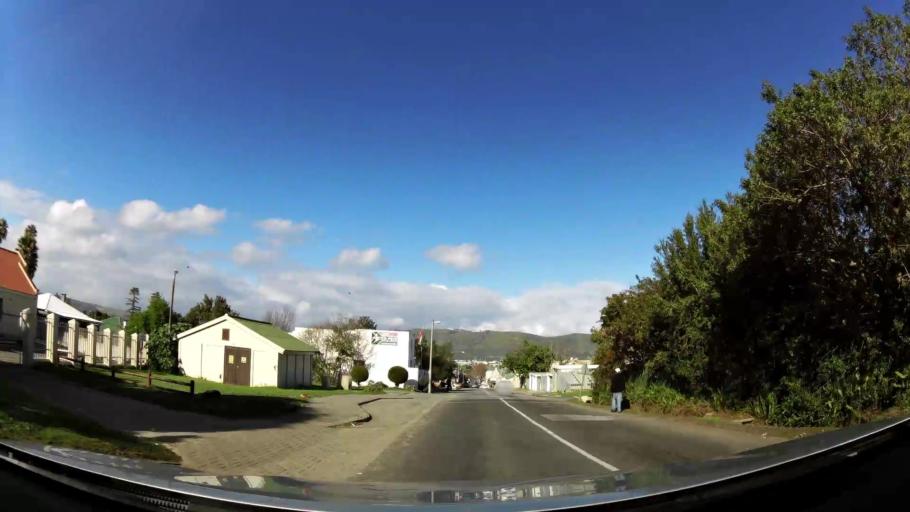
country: ZA
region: Western Cape
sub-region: Eden District Municipality
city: Knysna
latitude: -34.0332
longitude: 23.0470
